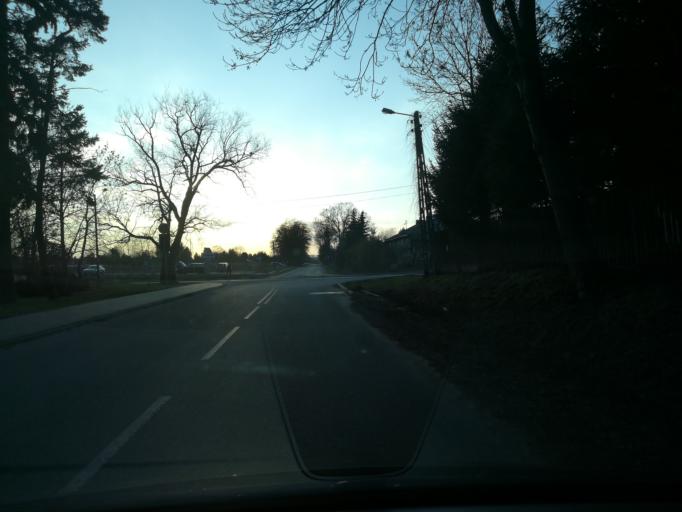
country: PL
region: Lodz Voivodeship
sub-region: Piotrkow Trybunalski
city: Piotrkow Trybunalski
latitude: 51.4058
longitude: 19.6476
